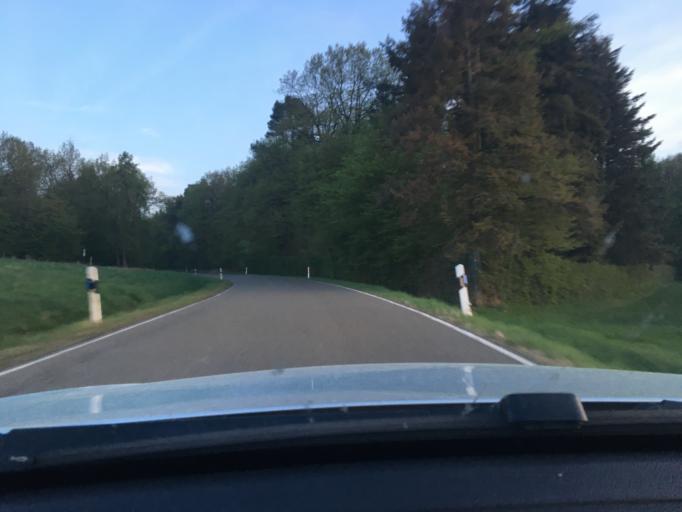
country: DE
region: Rheinland-Pfalz
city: Kriegsfeld
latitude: 49.7029
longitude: 7.9115
